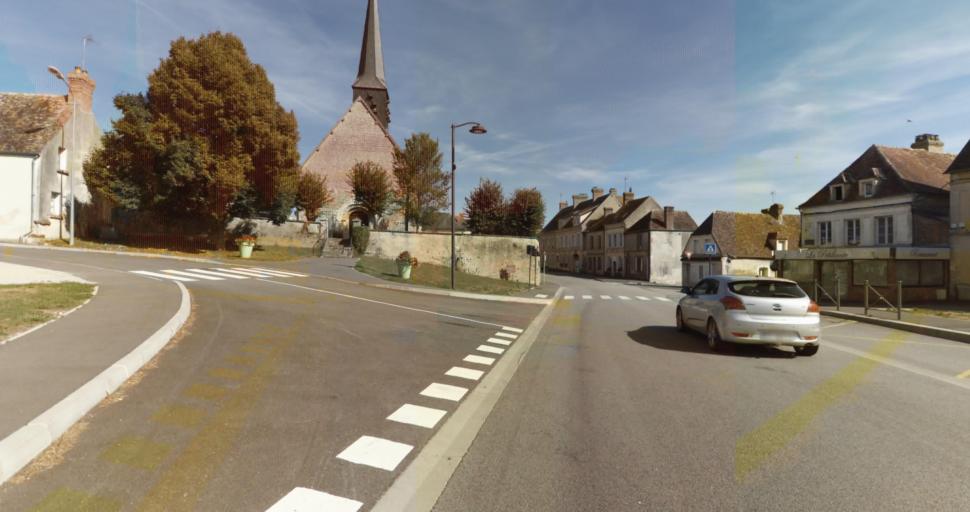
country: FR
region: Lower Normandy
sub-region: Departement de l'Orne
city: Sees
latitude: 48.7066
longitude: 0.2172
